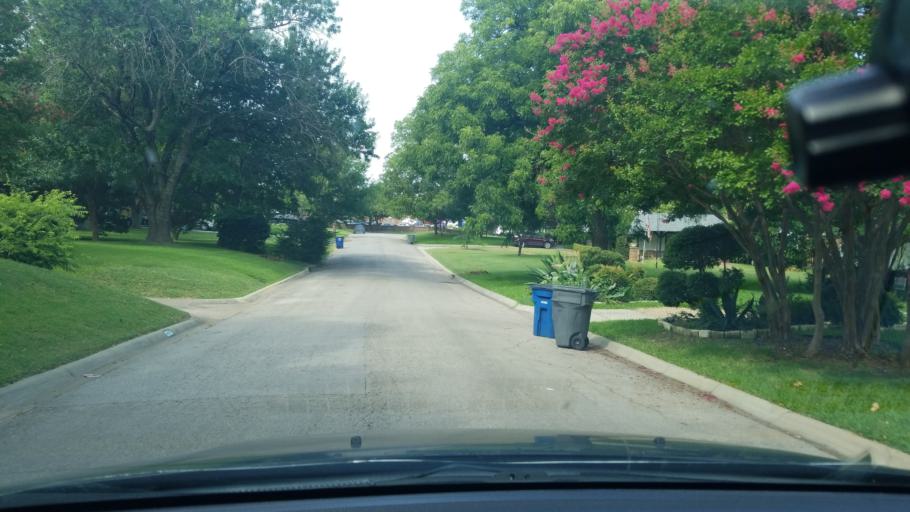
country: US
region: Texas
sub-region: Dallas County
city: Highland Park
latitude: 32.8306
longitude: -96.7049
